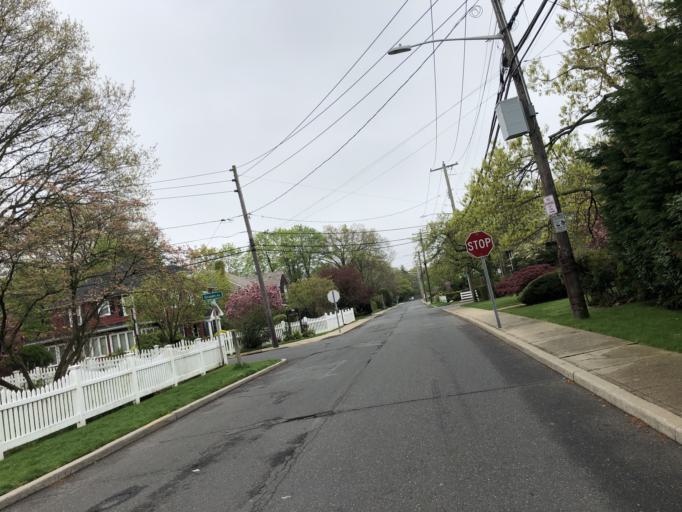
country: US
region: New York
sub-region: Nassau County
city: Woodmere
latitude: 40.6275
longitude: -73.7027
